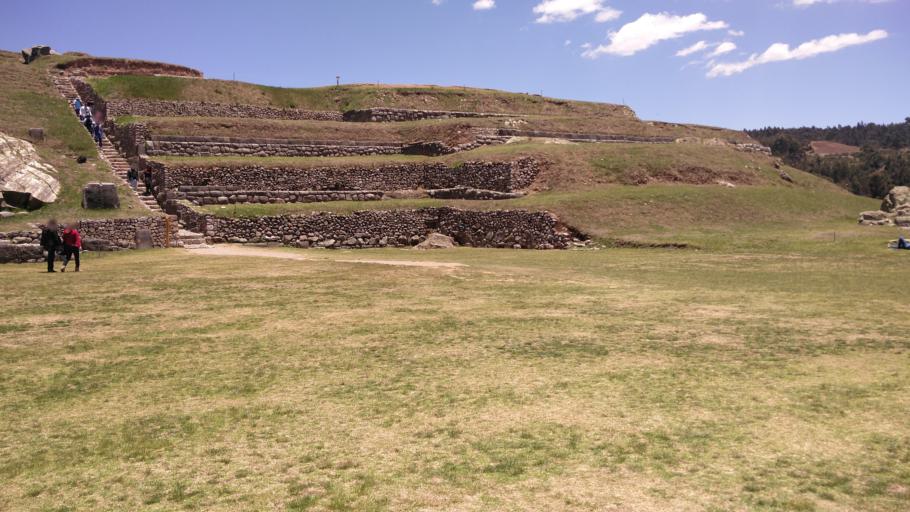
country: PE
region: Cusco
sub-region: Provincia de Cusco
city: Cusco
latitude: -13.5079
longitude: -71.9819
